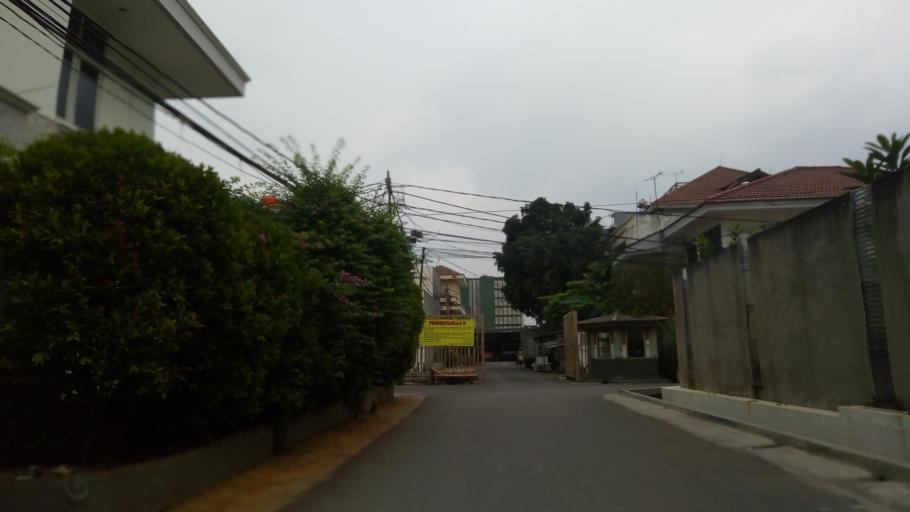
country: ID
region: Jakarta Raya
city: Jakarta
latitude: -6.1557
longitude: 106.8391
